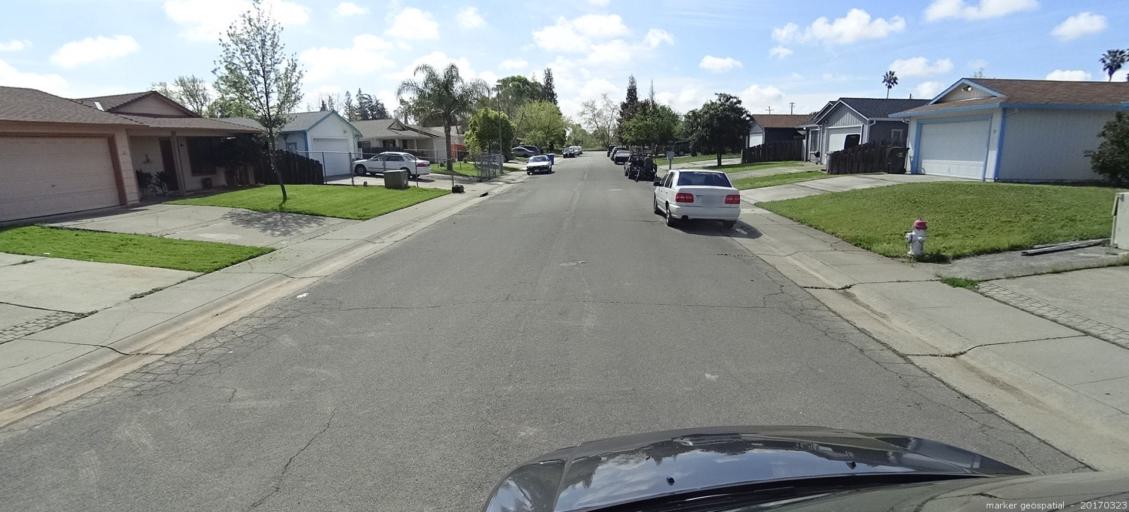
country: US
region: California
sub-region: Sacramento County
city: Florin
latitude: 38.5173
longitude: -121.4329
